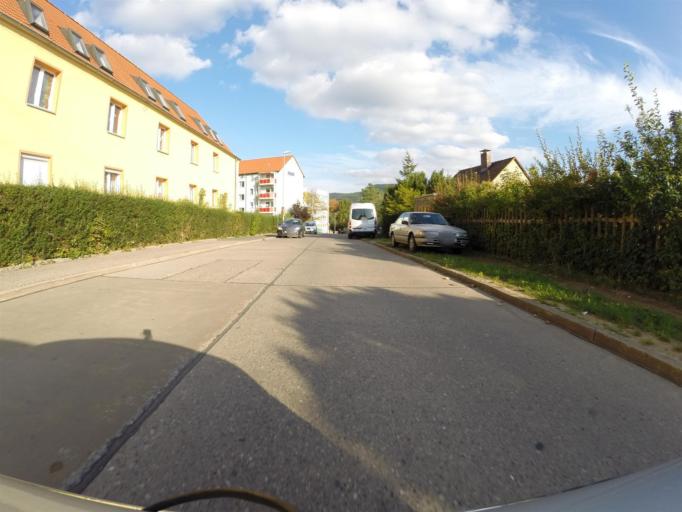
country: DE
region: Thuringia
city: Jena
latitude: 50.9514
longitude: 11.6071
